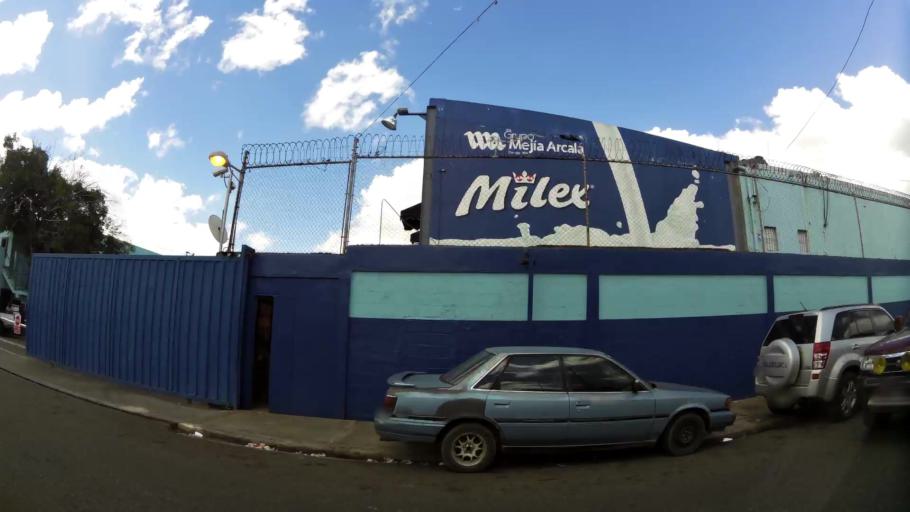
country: DO
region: Nacional
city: Ensanche Luperon
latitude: 18.4948
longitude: -69.9103
